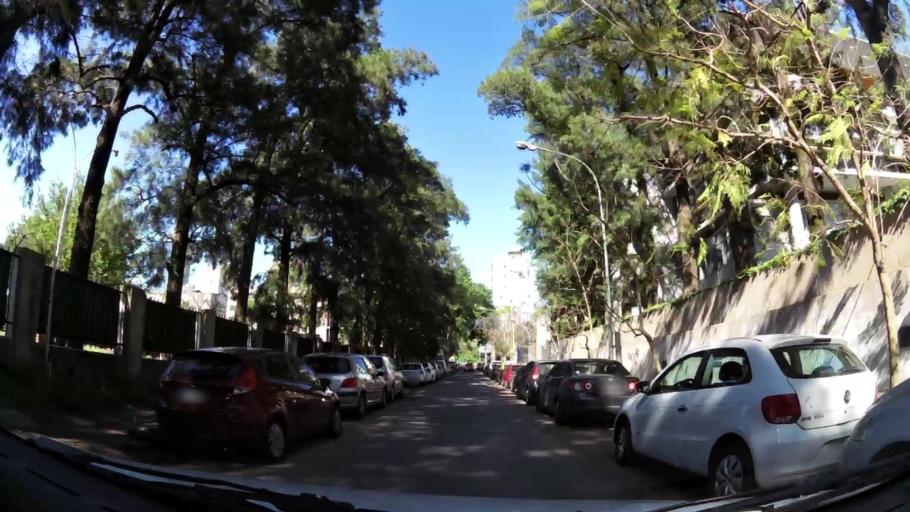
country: AR
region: Buenos Aires
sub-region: Partido de Vicente Lopez
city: Olivos
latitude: -34.5259
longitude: -58.4700
